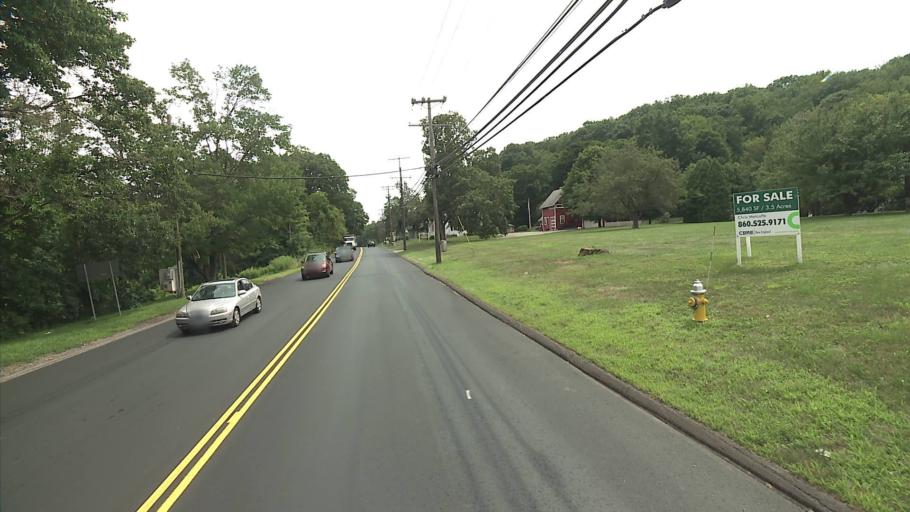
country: US
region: Connecticut
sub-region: New Haven County
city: Seymour
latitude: 41.4042
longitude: -73.0921
